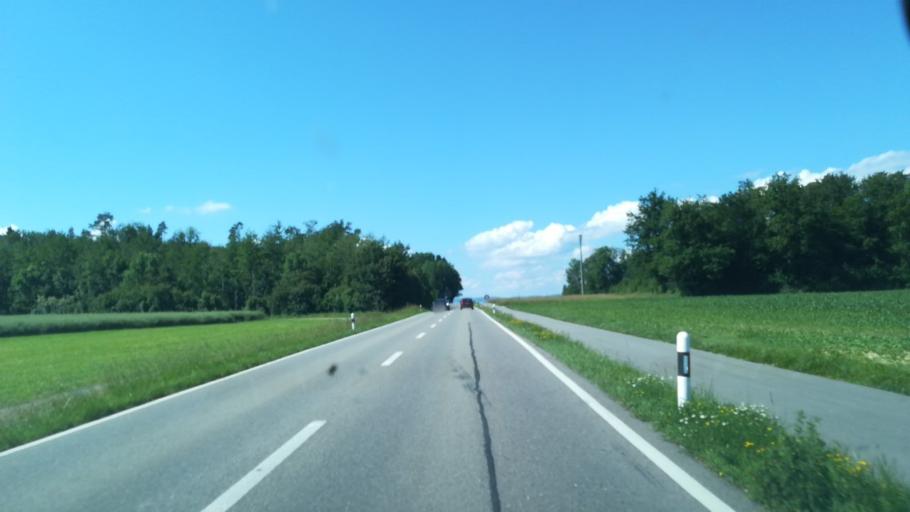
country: CH
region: Thurgau
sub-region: Kreuzlingen District
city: Kreuzlingen
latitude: 47.6207
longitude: 9.1685
